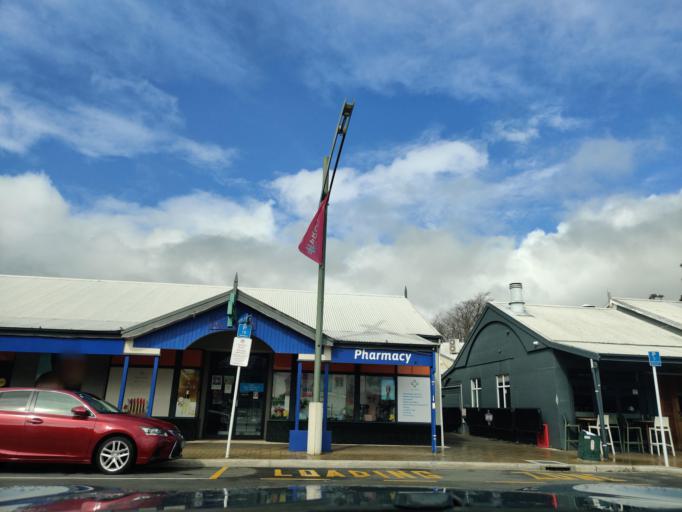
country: NZ
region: Hawke's Bay
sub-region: Hastings District
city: Hastings
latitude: -39.6693
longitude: 176.8780
